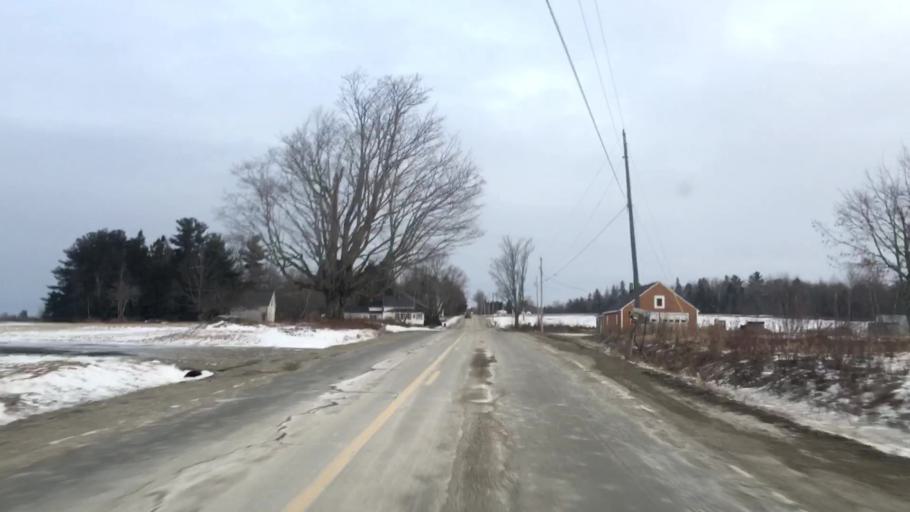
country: US
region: Maine
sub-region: Hancock County
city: Franklin
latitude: 44.7090
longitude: -68.3394
